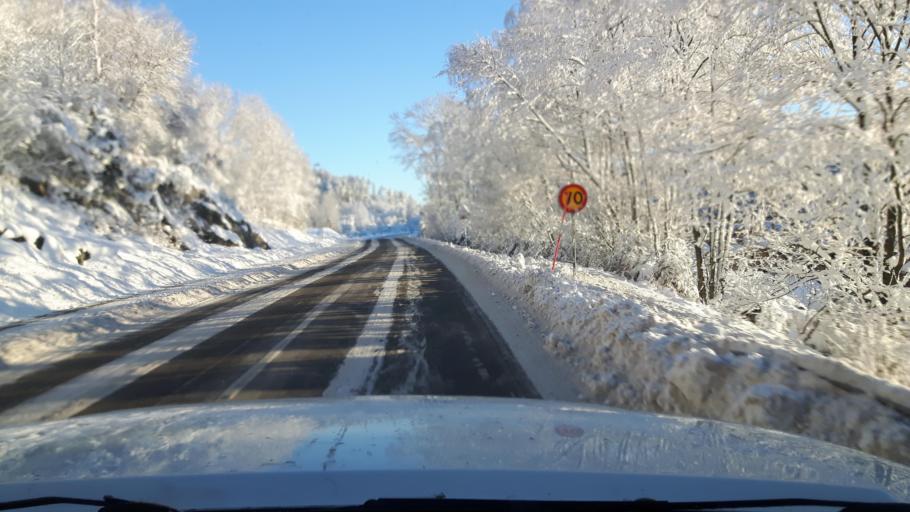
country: SE
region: Halland
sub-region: Kungsbacka Kommun
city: Fjaeras kyrkby
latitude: 57.5477
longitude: 12.1786
